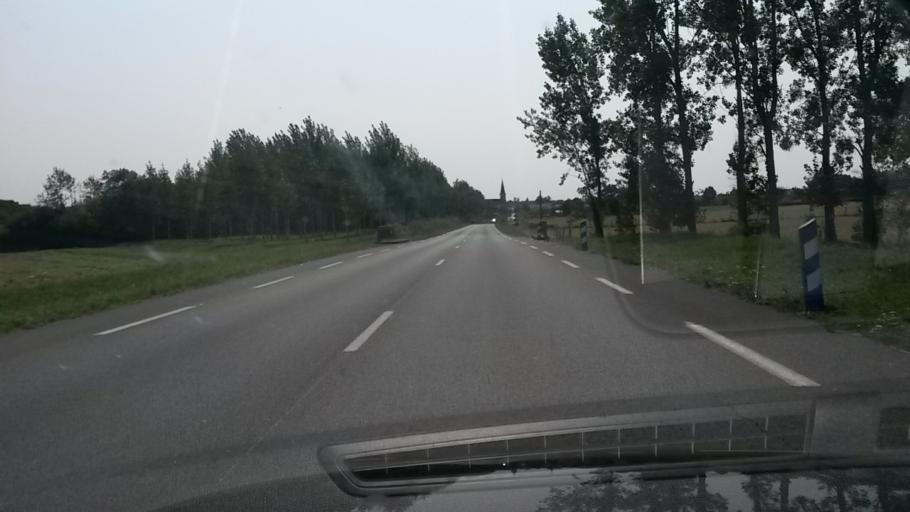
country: FR
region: Pays de la Loire
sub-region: Departement de la Mayenne
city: Chemaze
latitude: 47.7593
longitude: -0.7880
